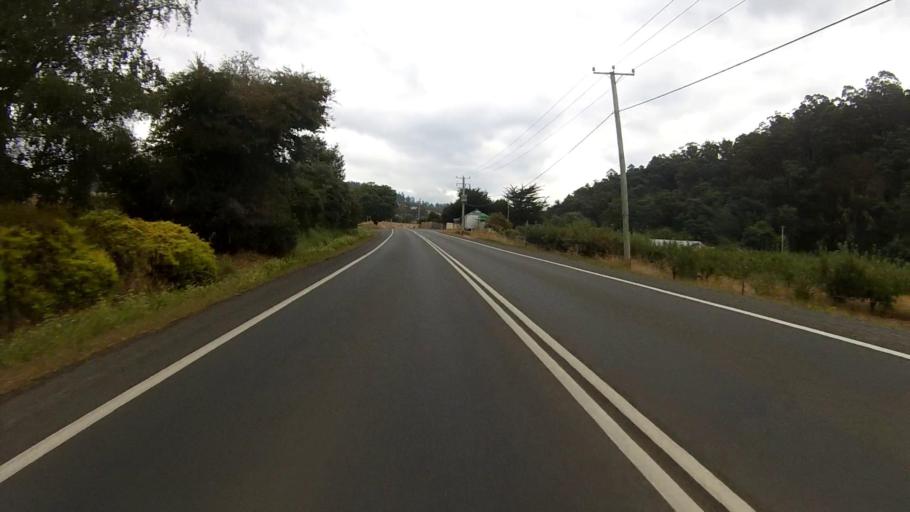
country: AU
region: Tasmania
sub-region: Huon Valley
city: Cygnet
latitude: -43.1406
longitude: 147.0627
